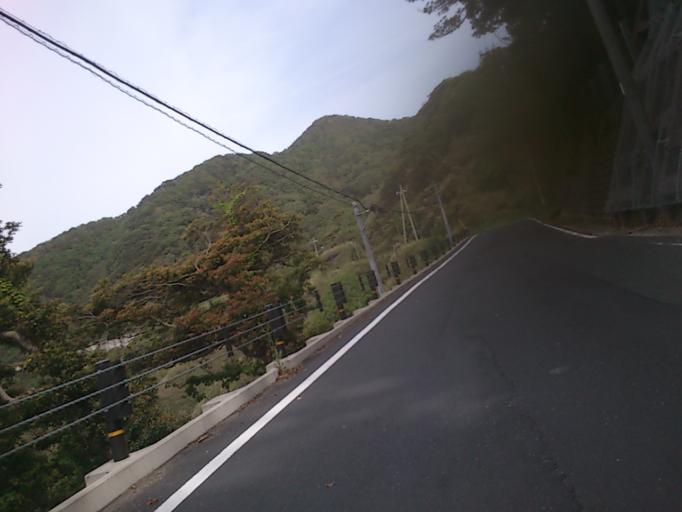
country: JP
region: Hyogo
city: Toyooka
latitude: 35.6912
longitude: 134.9979
